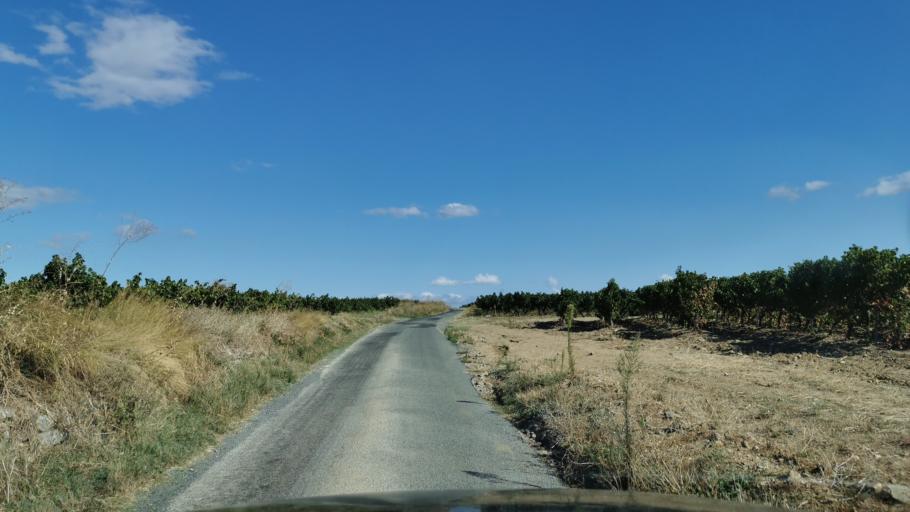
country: FR
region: Languedoc-Roussillon
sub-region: Departement de l'Aude
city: Ginestas
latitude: 43.2651
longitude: 2.8437
